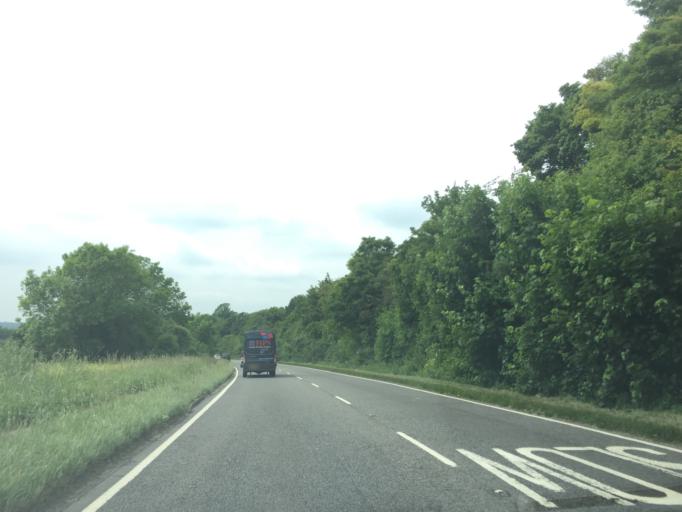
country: GB
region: England
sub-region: Hampshire
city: Kings Worthy
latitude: 51.0595
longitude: -1.2830
